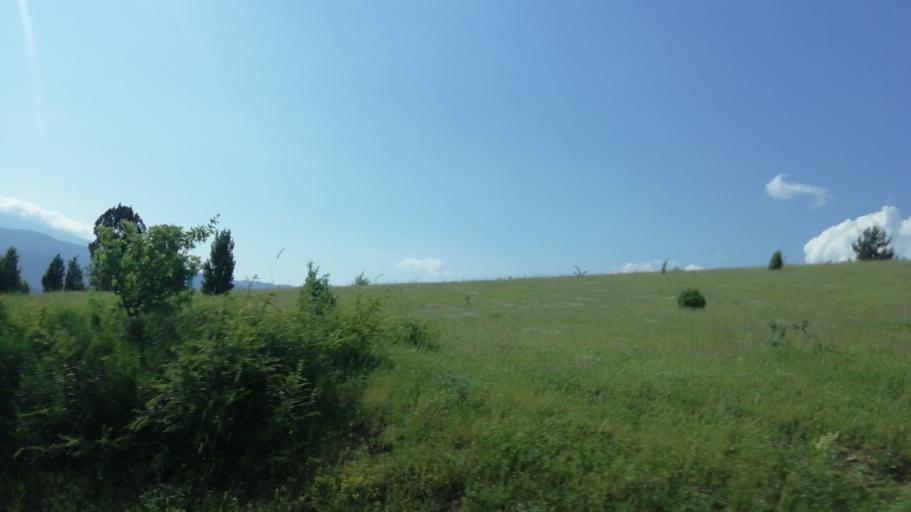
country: TR
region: Karabuk
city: Karabuk
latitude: 41.1303
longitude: 32.5699
